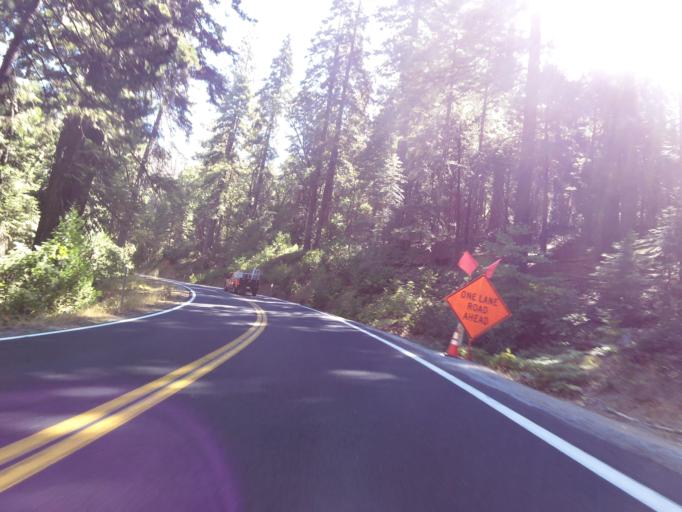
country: US
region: California
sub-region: Calaveras County
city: Arnold
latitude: 38.2693
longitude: -120.3243
